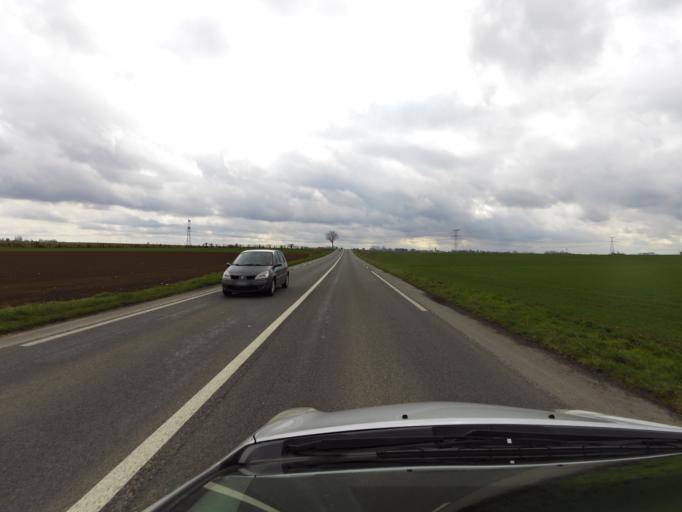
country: FR
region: Nord-Pas-de-Calais
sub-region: Departement du Pas-de-Calais
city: Beaurains
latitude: 50.2513
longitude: 2.7917
